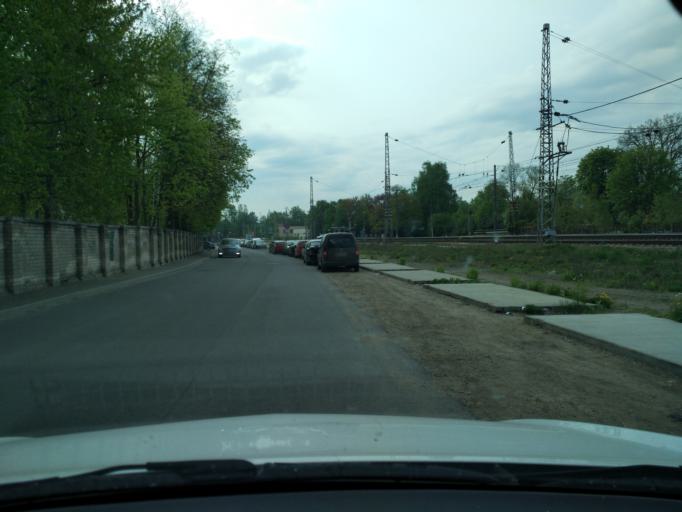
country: LV
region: Marupe
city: Marupe
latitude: 56.9304
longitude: 24.0620
